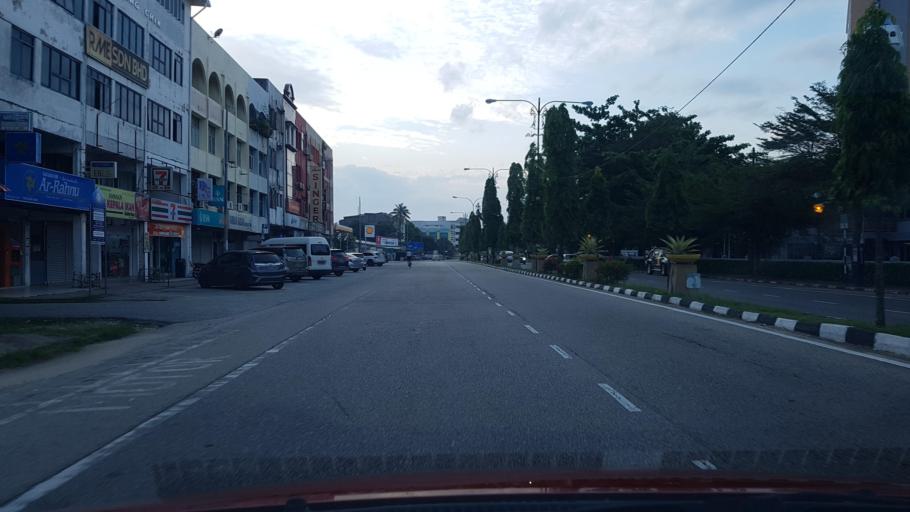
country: MY
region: Terengganu
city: Kuala Terengganu
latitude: 5.3260
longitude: 103.1484
